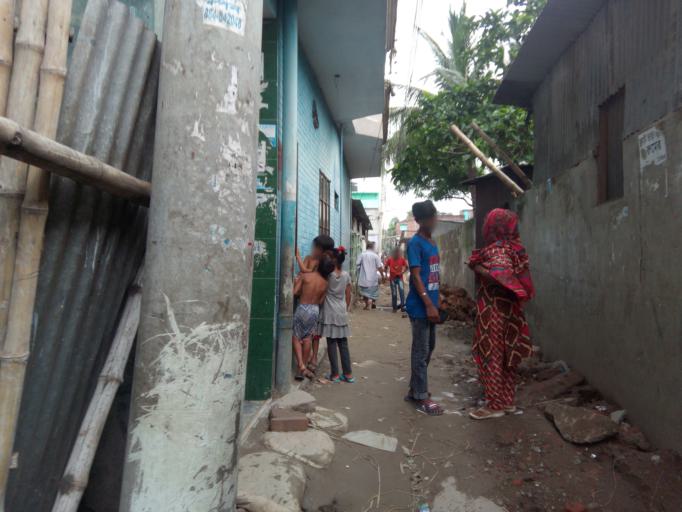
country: BD
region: Dhaka
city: Azimpur
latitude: 23.7177
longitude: 90.3757
